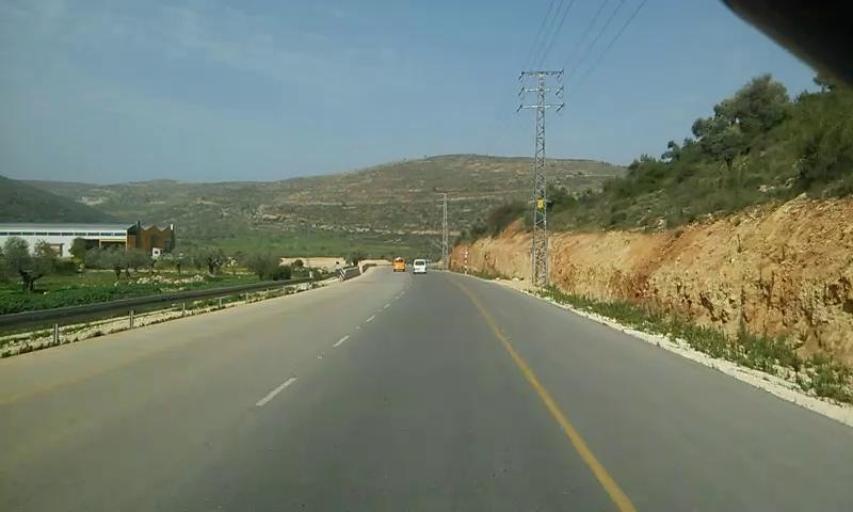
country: PS
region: West Bank
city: Dura al Qar`
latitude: 31.9859
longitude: 35.2295
